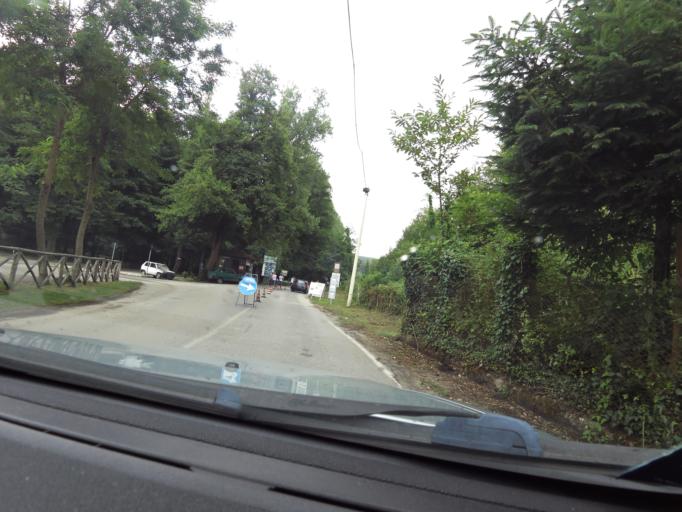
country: IT
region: Calabria
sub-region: Provincia di Vibo-Valentia
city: Serra San Bruno
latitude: 38.5589
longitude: 16.3144
